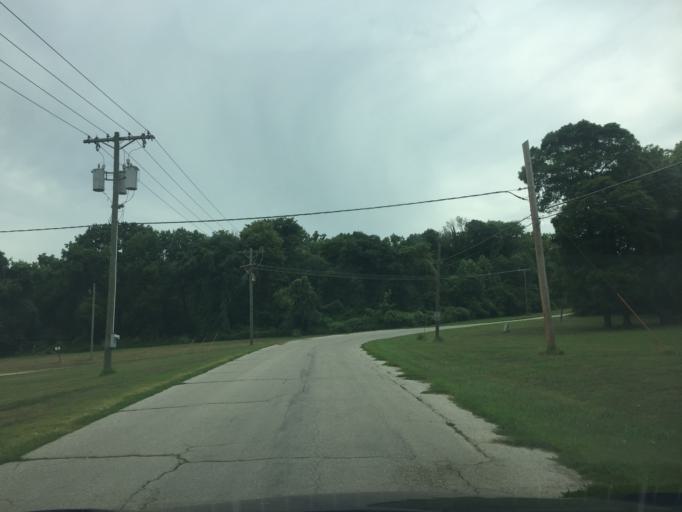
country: US
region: Kansas
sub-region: Leavenworth County
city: Leavenworth
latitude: 39.3593
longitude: -94.9302
